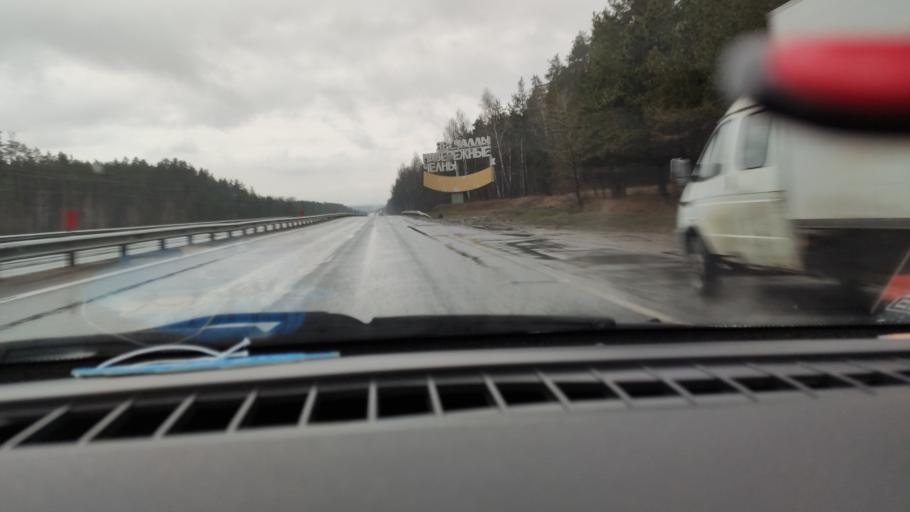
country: RU
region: Tatarstan
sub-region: Tukayevskiy Rayon
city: Naberezhnyye Chelny
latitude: 55.7332
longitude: 52.2530
